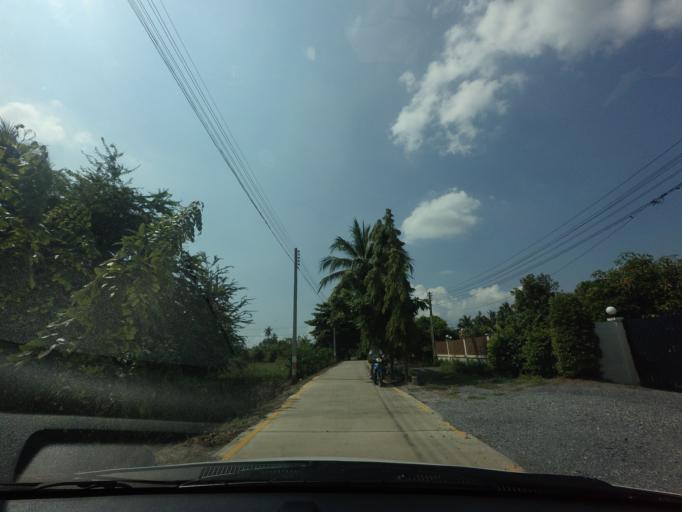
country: TH
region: Nakhon Pathom
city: Nakhon Chai Si
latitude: 13.8080
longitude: 100.1886
